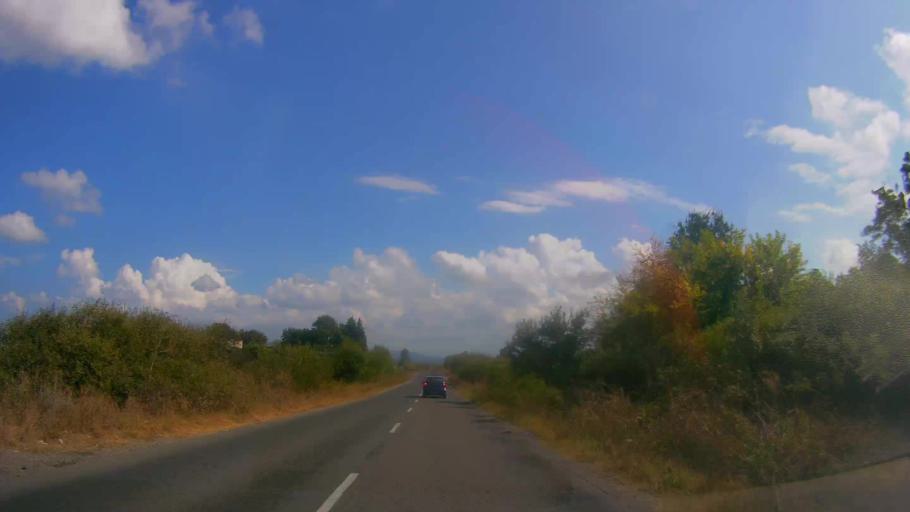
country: BG
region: Burgas
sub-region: Obshtina Burgas
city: Burgas
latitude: 42.4752
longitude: 27.4166
